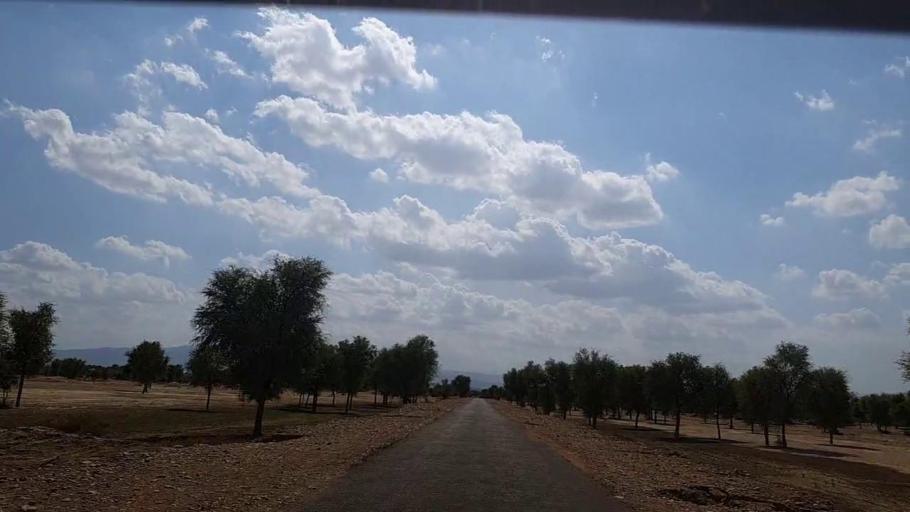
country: PK
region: Sindh
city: Johi
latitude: 26.5205
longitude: 67.4620
